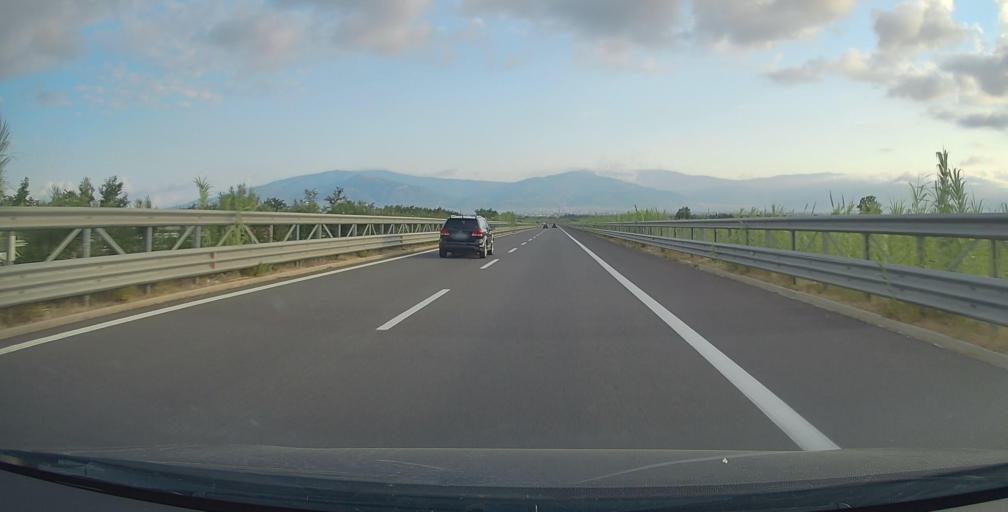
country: IT
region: Calabria
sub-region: Provincia di Catanzaro
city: Acconia
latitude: 38.8765
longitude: 16.2816
